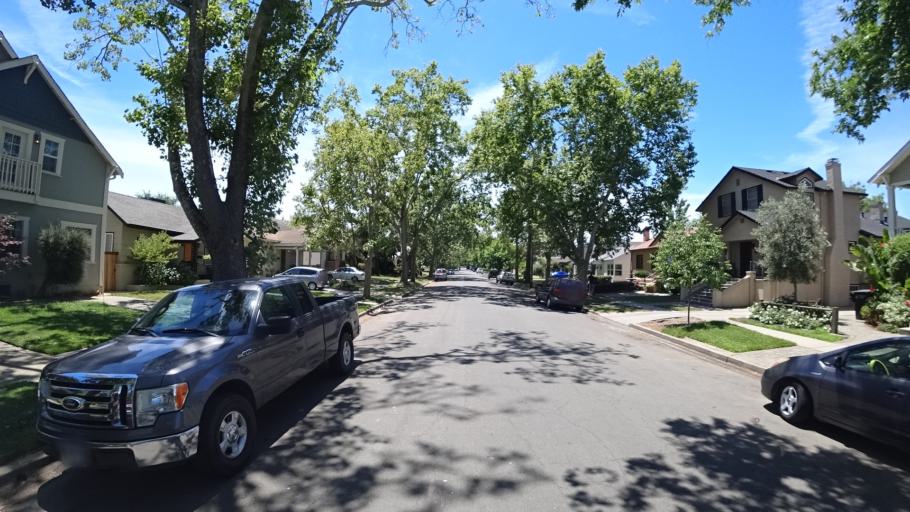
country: US
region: California
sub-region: Sacramento County
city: Sacramento
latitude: 38.5655
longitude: -121.4618
